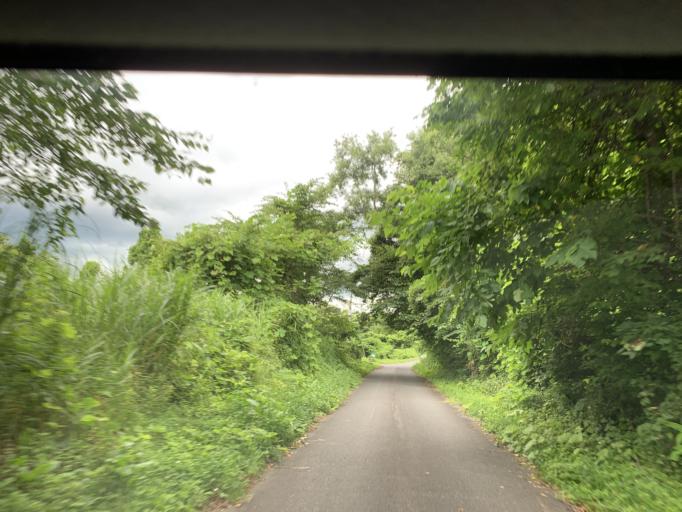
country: JP
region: Iwate
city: Ichinoseki
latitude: 38.9680
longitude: 140.9944
